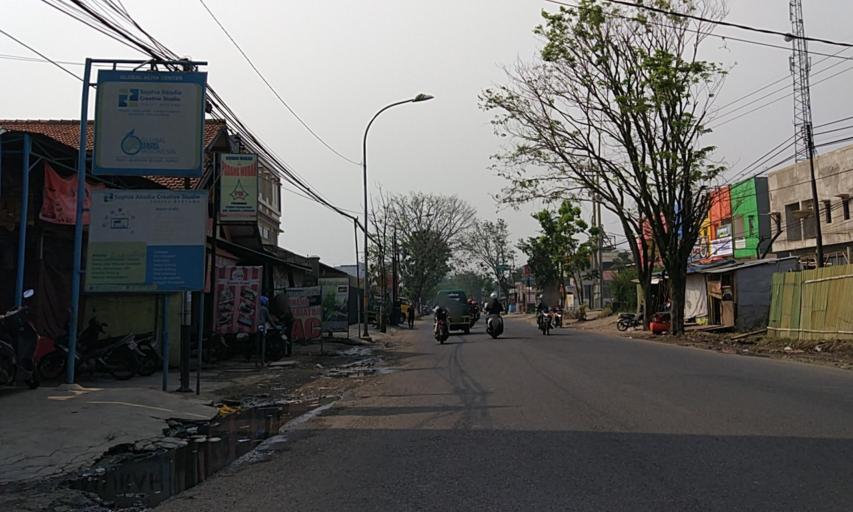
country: ID
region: West Java
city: Margahayukencana
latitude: -7.0053
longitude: 107.5519
